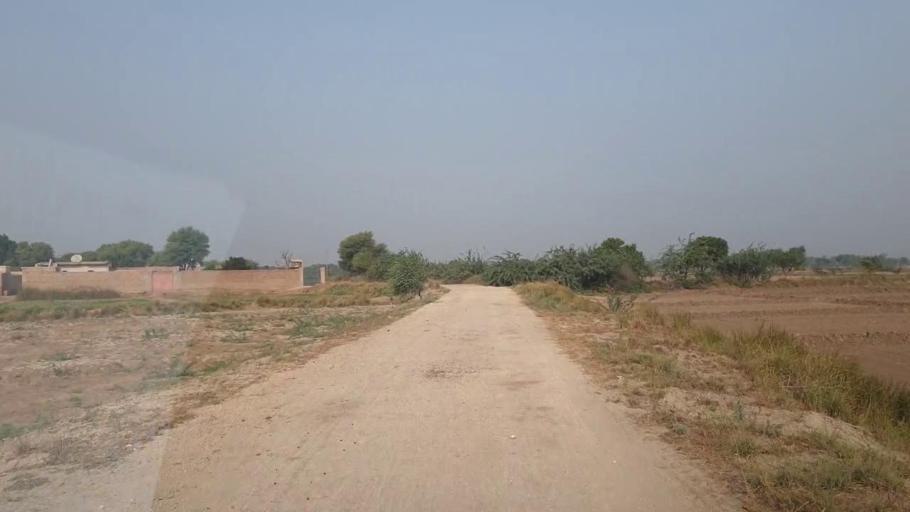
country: PK
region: Sindh
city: Tando Jam
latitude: 25.3298
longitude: 68.5235
